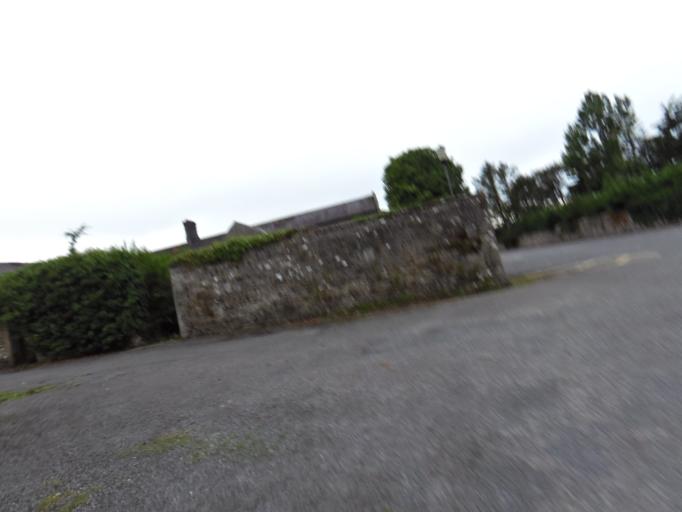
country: IE
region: Connaught
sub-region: County Galway
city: Loughrea
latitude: 53.1909
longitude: -8.5635
